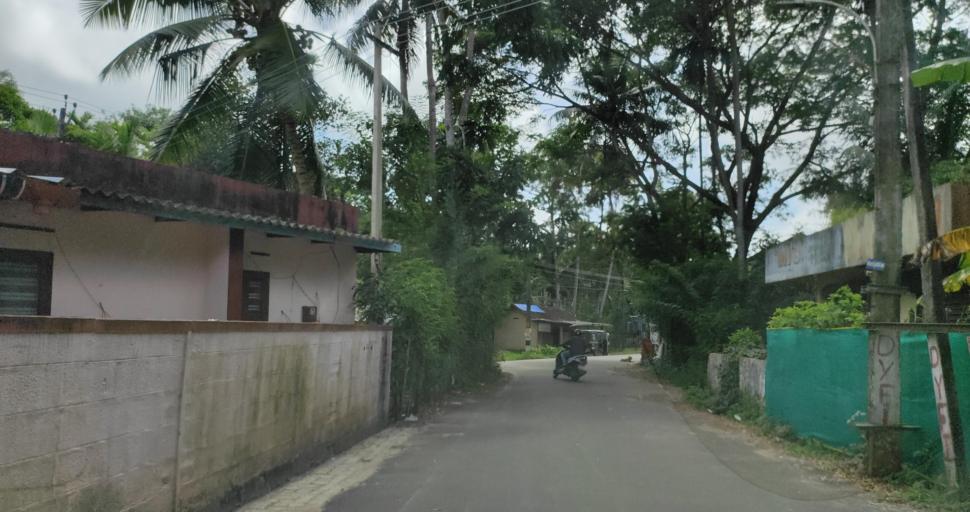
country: IN
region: Kerala
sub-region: Alappuzha
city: Shertallai
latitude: 9.6566
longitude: 76.3685
